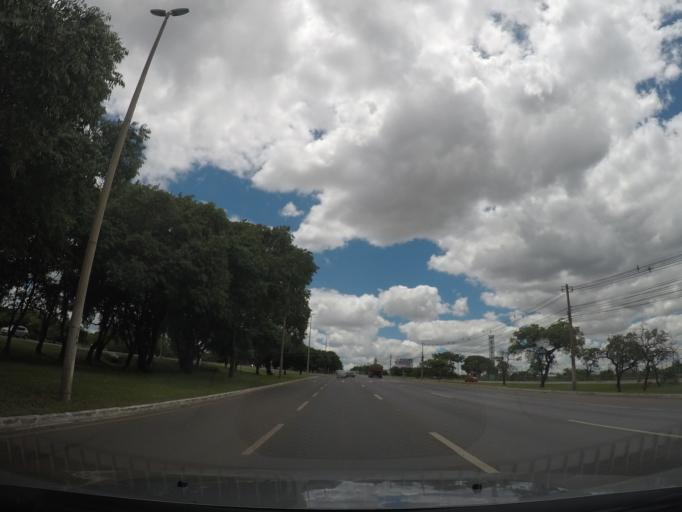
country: BR
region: Federal District
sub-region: Brasilia
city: Brasilia
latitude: -15.7536
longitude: -47.9255
